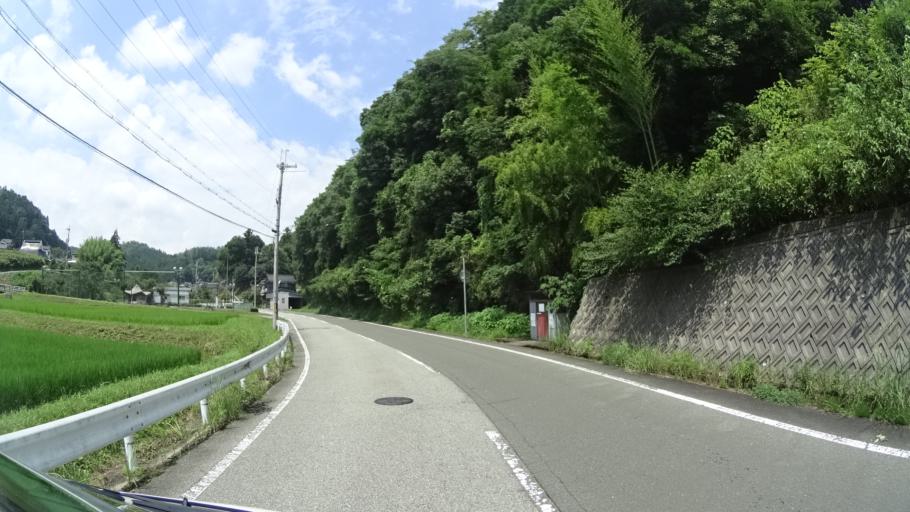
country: JP
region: Hyogo
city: Sasayama
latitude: 35.1698
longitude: 135.2544
